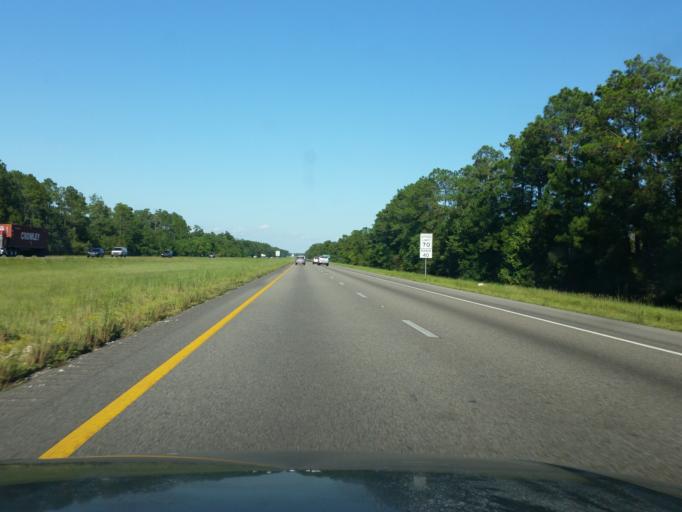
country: US
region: Mississippi
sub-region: Hancock County
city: Diamondhead
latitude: 30.3758
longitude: -89.3662
